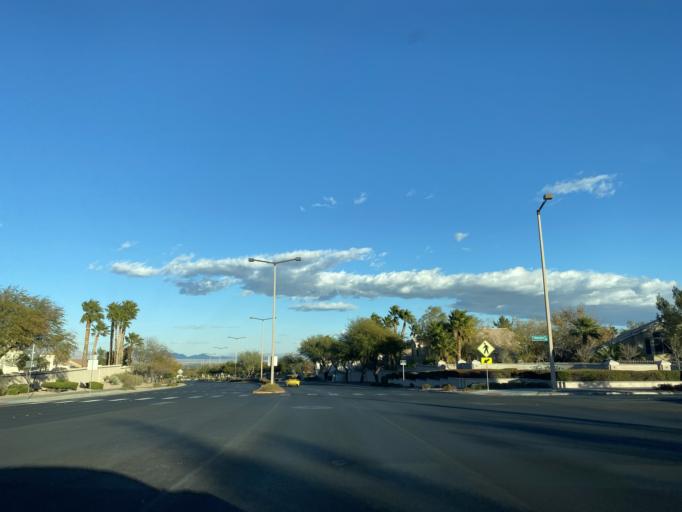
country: US
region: Nevada
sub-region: Clark County
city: Summerlin South
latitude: 36.2043
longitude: -115.3091
